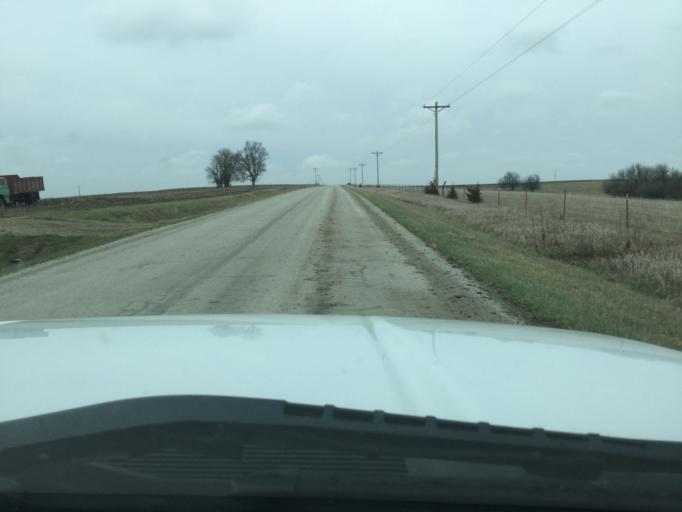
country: US
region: Kansas
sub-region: Nemaha County
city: Sabetha
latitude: 39.8742
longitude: -95.7141
